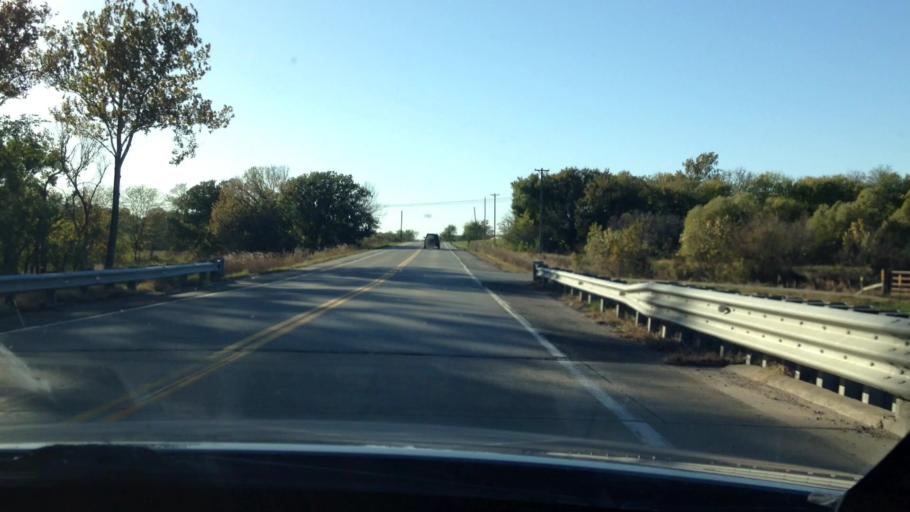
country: US
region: Kansas
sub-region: Johnson County
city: Edgerton
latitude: 38.7677
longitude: -94.9829
